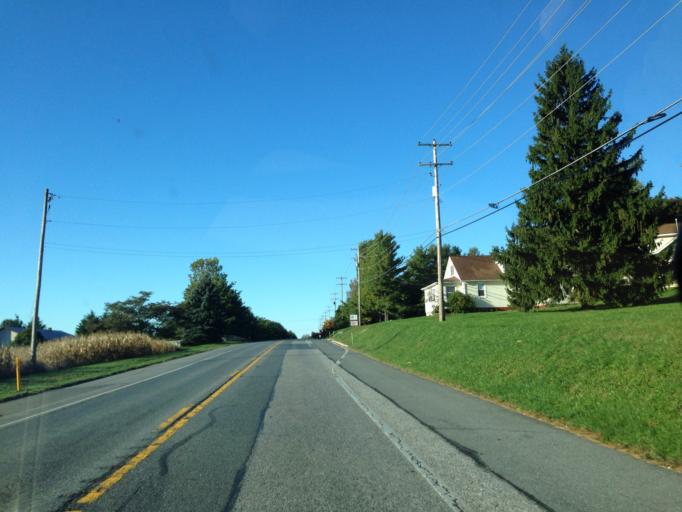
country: US
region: Maryland
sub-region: Carroll County
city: Mount Airy
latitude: 39.4164
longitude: -77.1205
